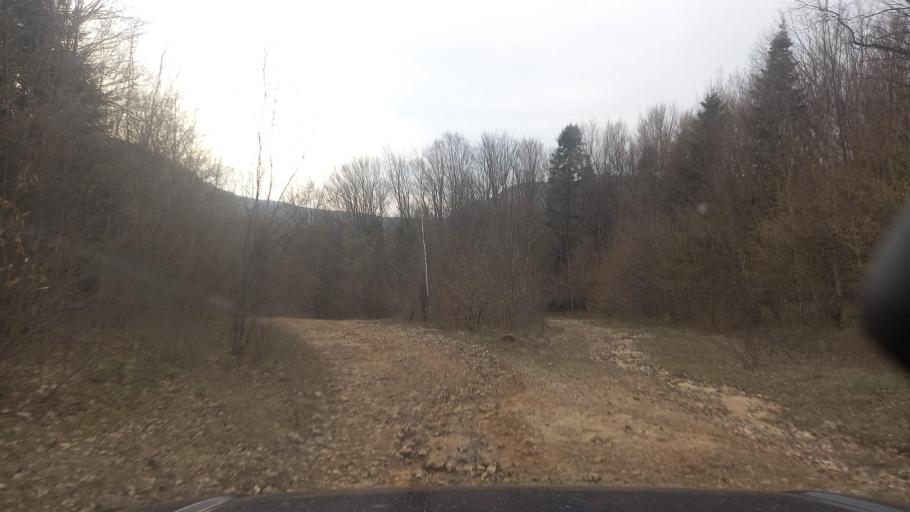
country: RU
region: Adygeya
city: Kamennomostskiy
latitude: 44.1887
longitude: 39.9721
